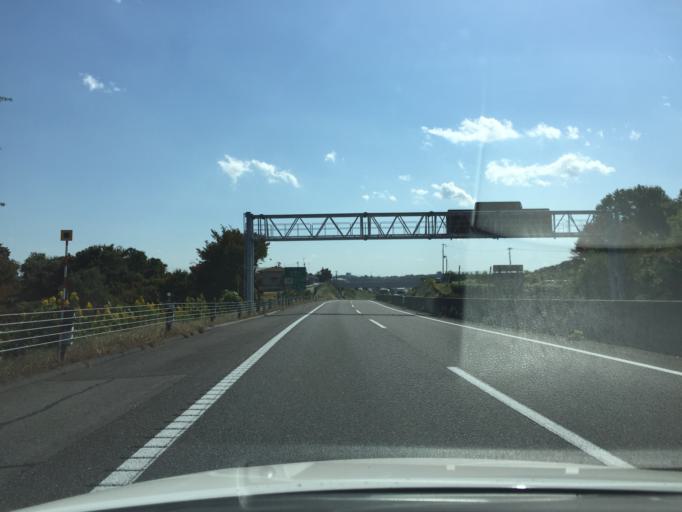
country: JP
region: Fukushima
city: Sukagawa
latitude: 37.3017
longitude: 140.3503
